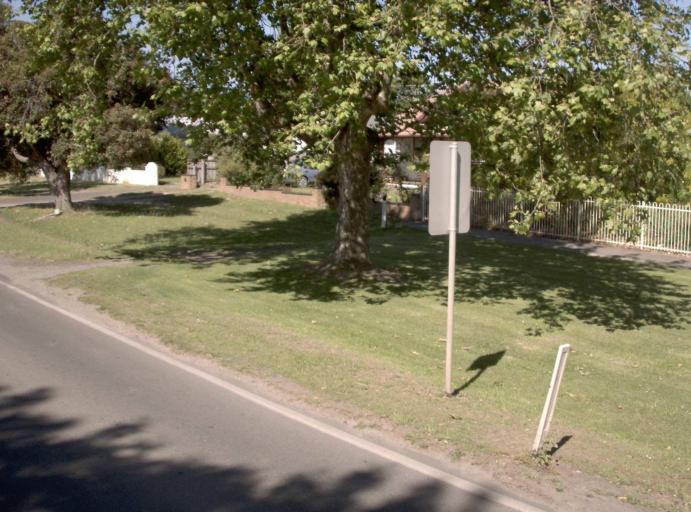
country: AU
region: Victoria
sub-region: Latrobe
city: Traralgon
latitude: -38.5563
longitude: 146.6776
